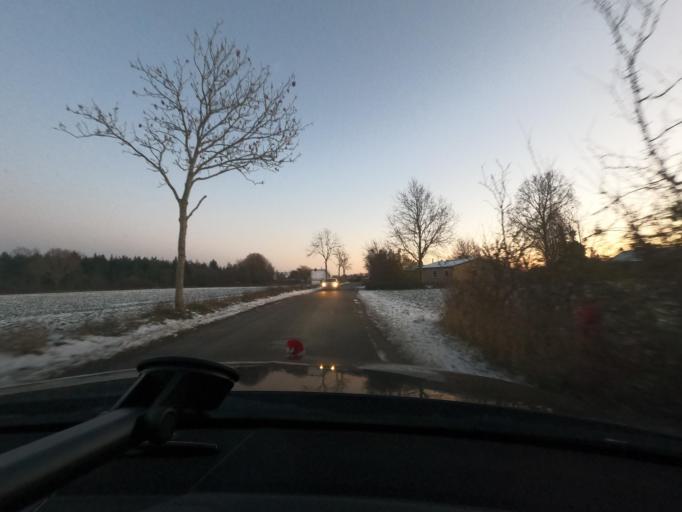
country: DK
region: South Denmark
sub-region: Sonderborg Kommune
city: Horuphav
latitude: 54.8706
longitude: 9.8945
